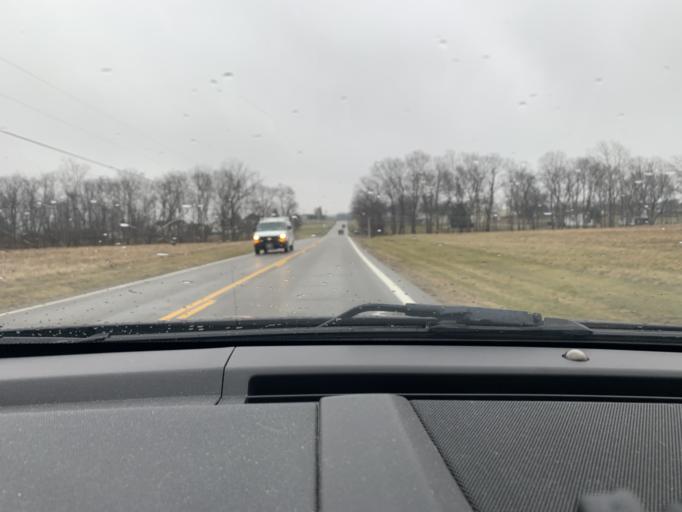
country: US
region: Ohio
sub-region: Ross County
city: Kingston
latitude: 39.4316
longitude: -82.9081
